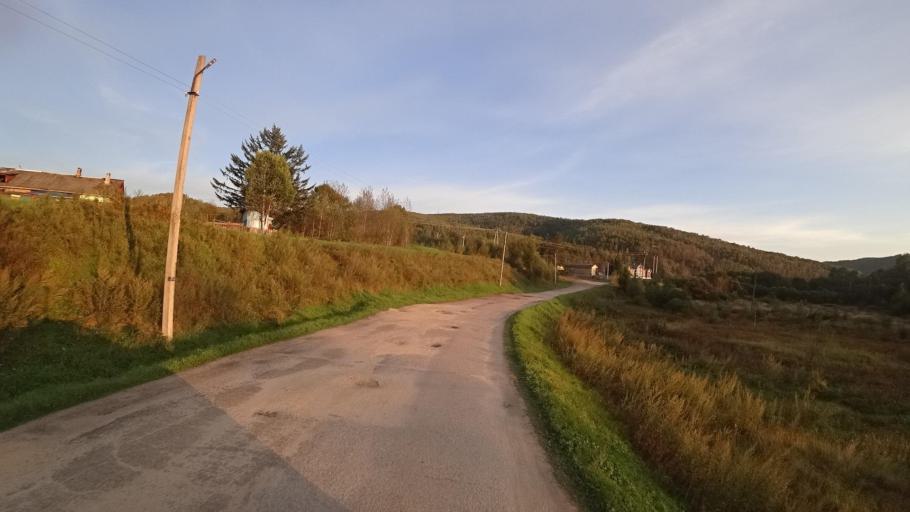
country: RU
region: Jewish Autonomous Oblast
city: Kul'dur
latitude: 49.1979
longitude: 131.6333
